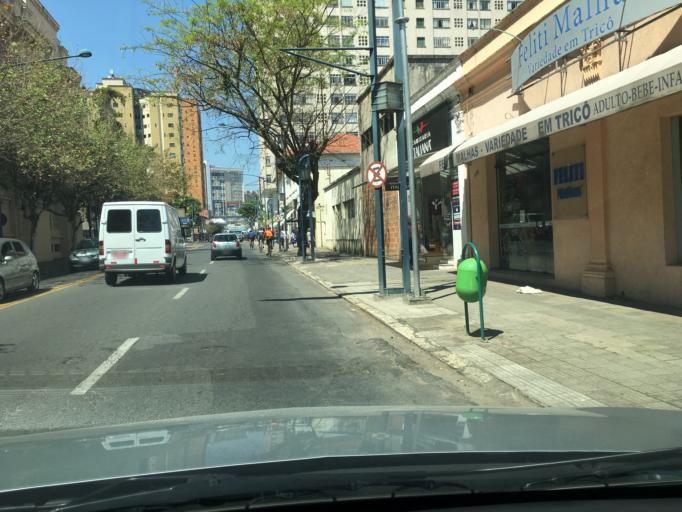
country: BR
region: Minas Gerais
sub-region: Pocos De Caldas
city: Pocos de Caldas
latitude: -21.7879
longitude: -46.5690
